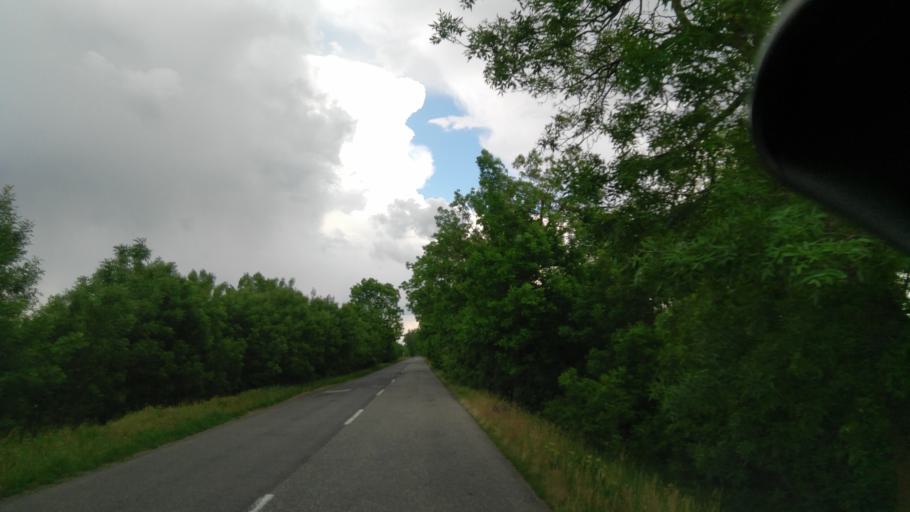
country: HU
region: Bekes
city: Fuzesgyarmat
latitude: 47.1544
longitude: 21.1156
